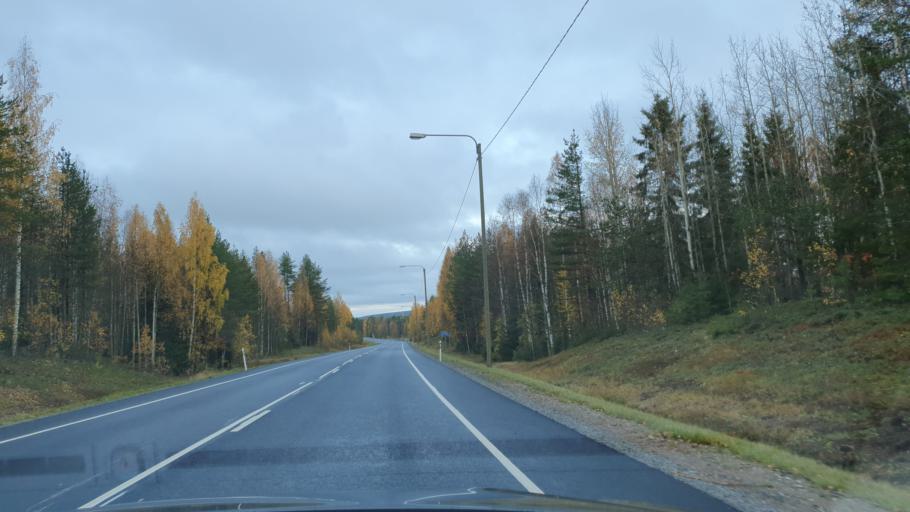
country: FI
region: Lapland
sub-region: Rovaniemi
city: Rovaniemi
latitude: 66.5407
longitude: 25.6589
